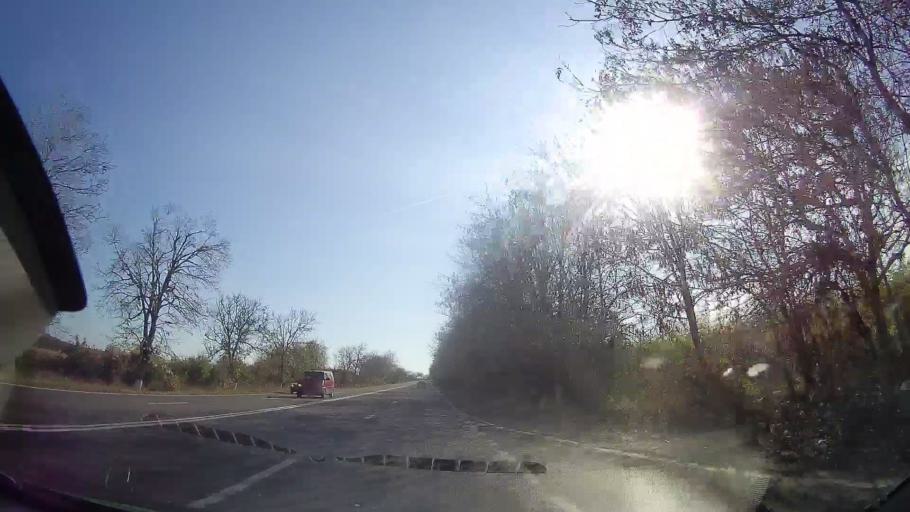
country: RO
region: Constanta
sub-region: Comuna Douazeci si Trei August
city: Douazeci si Trei August
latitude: 43.8909
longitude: 28.5724
